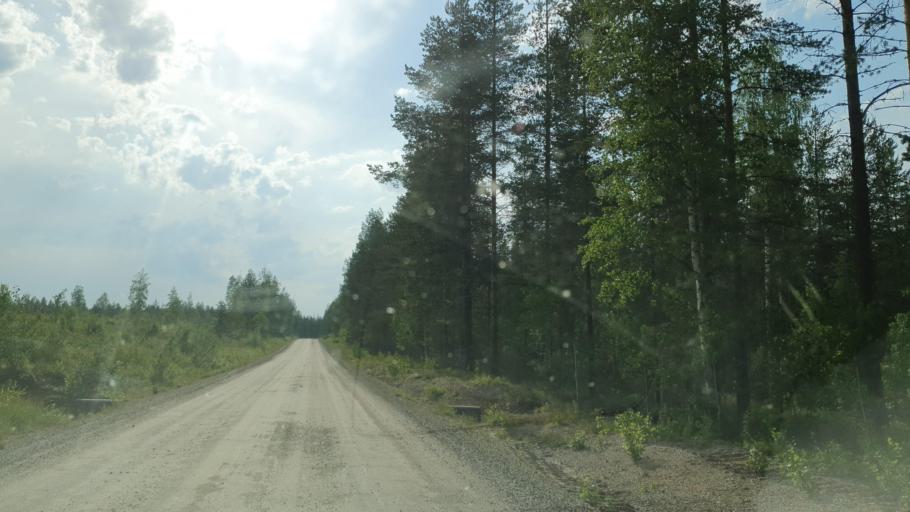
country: FI
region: Kainuu
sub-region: Kehys-Kainuu
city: Kuhmo
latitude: 64.0911
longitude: 29.5927
